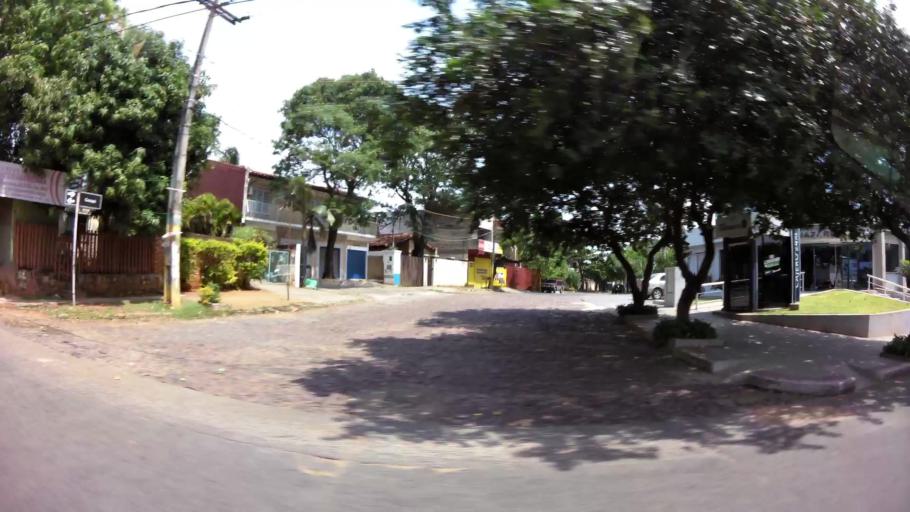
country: PY
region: Central
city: Lambare
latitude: -25.3182
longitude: -57.5992
